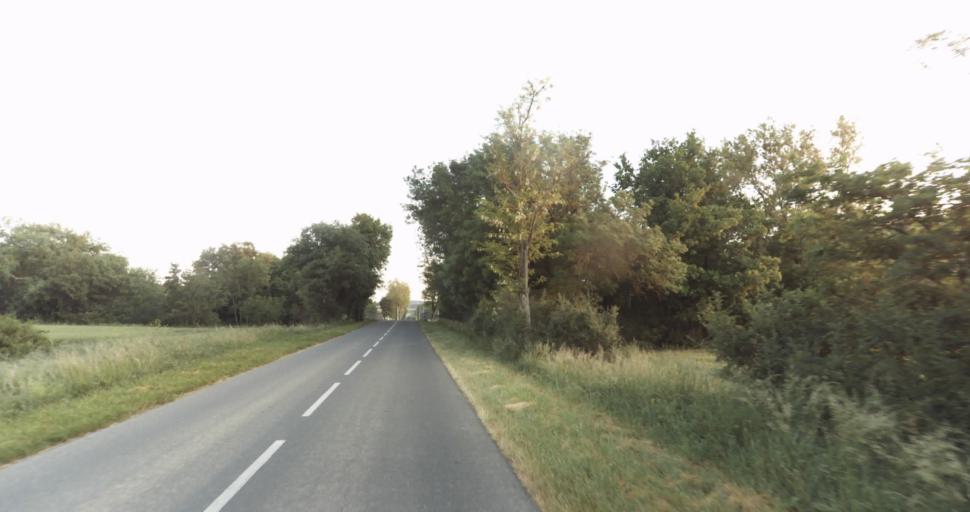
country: FR
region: Midi-Pyrenees
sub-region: Departement du Gers
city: Pujaudran
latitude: 43.6471
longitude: 1.1378
